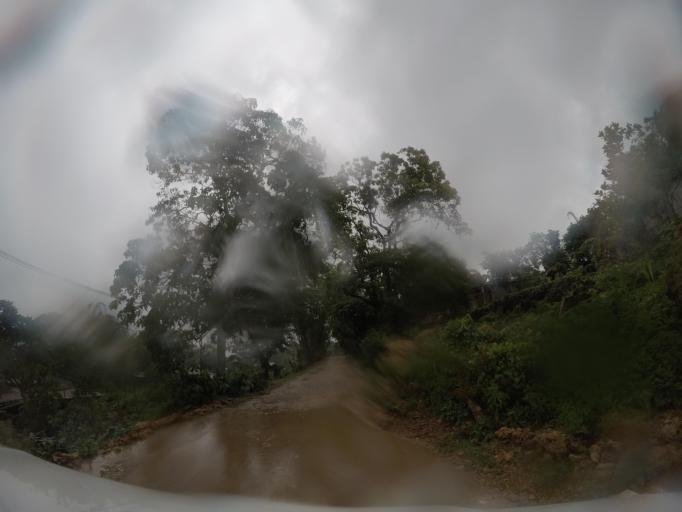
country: TL
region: Baucau
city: Venilale
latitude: -8.6425
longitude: 126.3967
